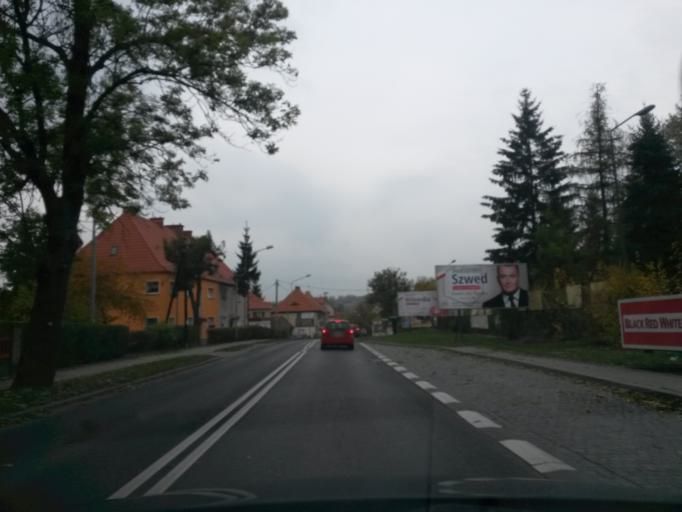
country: PL
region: Lower Silesian Voivodeship
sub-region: Powiat klodzki
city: Klodzko
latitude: 50.4287
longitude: 16.6576
